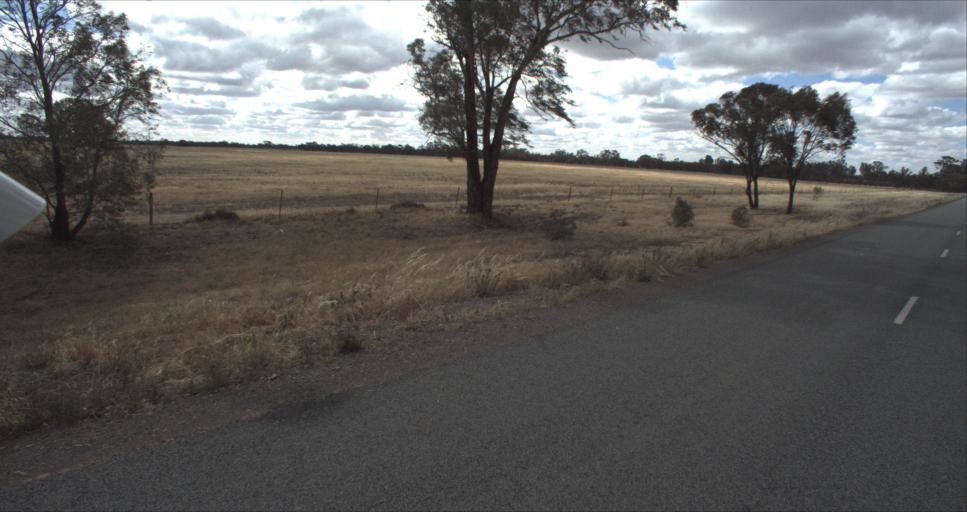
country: AU
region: New South Wales
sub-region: Leeton
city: Leeton
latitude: -34.6715
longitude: 146.3474
